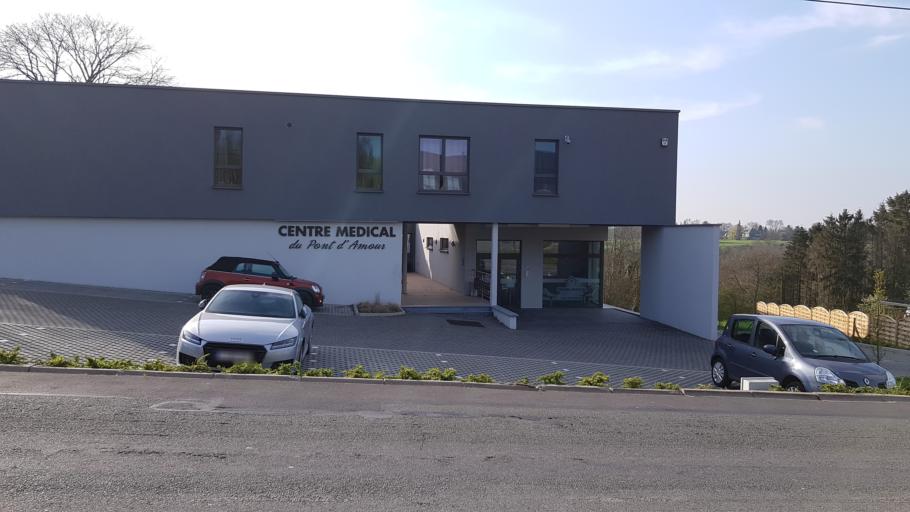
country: BE
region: Wallonia
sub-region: Province de Namur
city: Dinant
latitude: 50.2624
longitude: 4.9232
